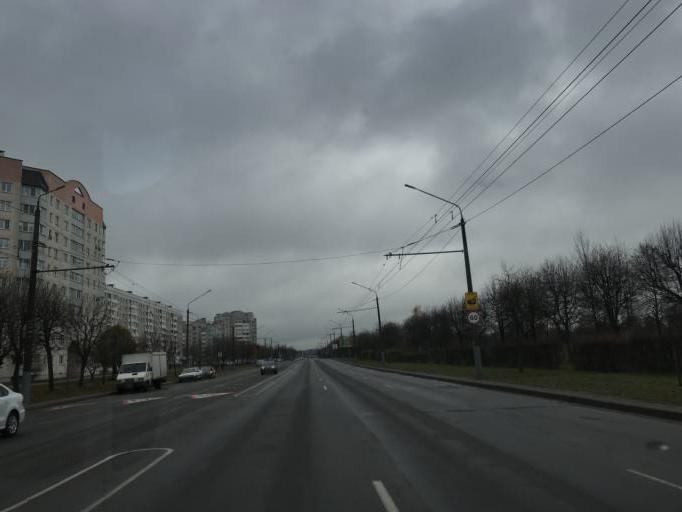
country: BY
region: Mogilev
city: Mahilyow
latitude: 53.8677
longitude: 30.3280
